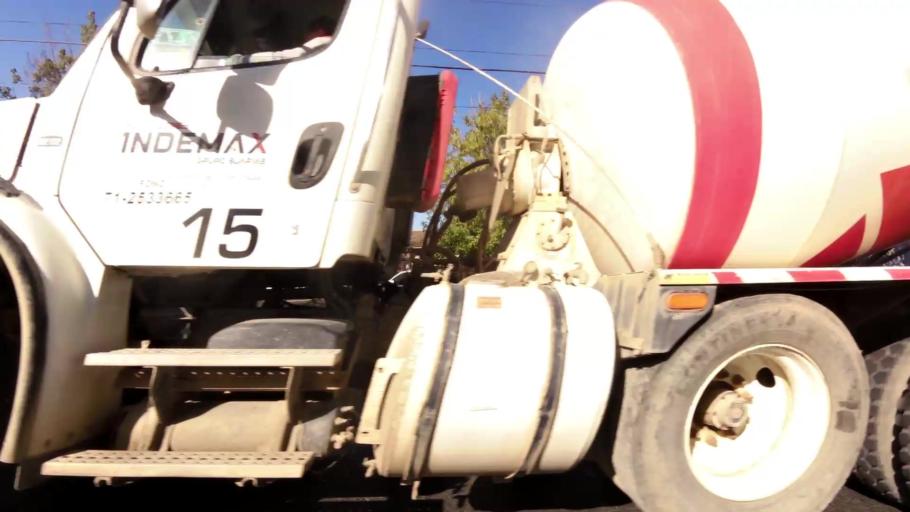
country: CL
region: Maule
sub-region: Provincia de Talca
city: Talca
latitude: -35.4192
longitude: -71.6523
